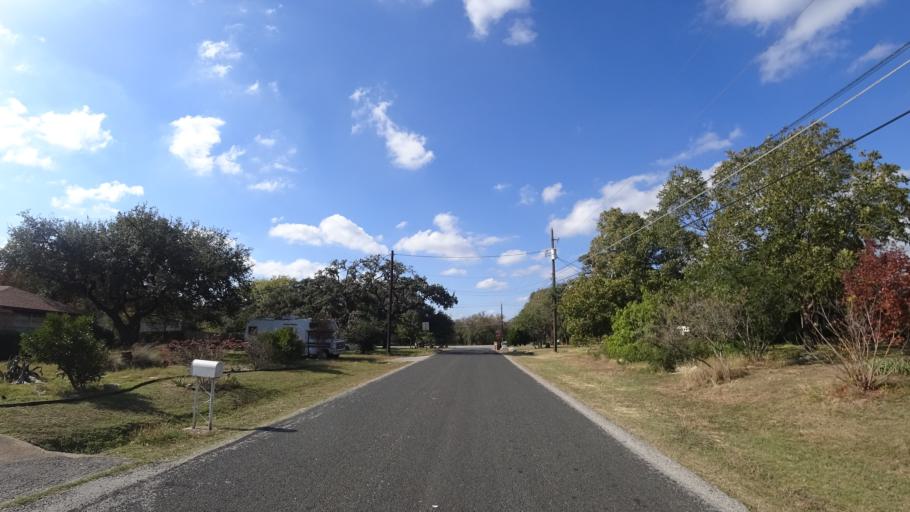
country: US
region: Texas
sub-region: Travis County
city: Shady Hollow
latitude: 30.1820
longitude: -97.8497
